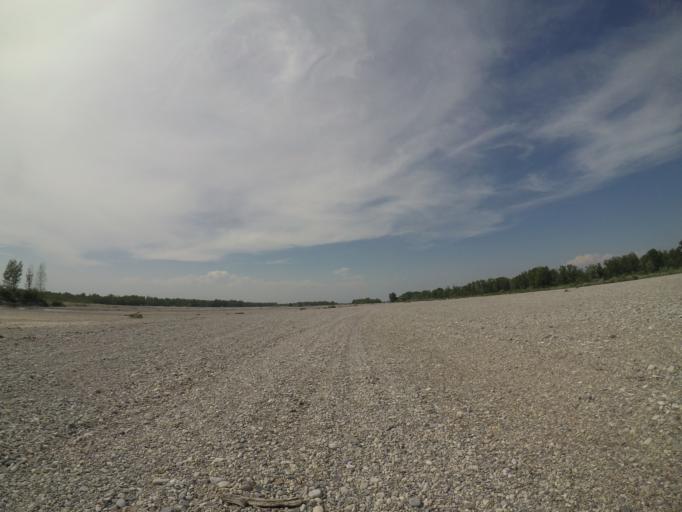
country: IT
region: Friuli Venezia Giulia
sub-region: Provincia di Udine
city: Camino al Tagliamento
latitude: 45.9073
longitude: 12.9218
